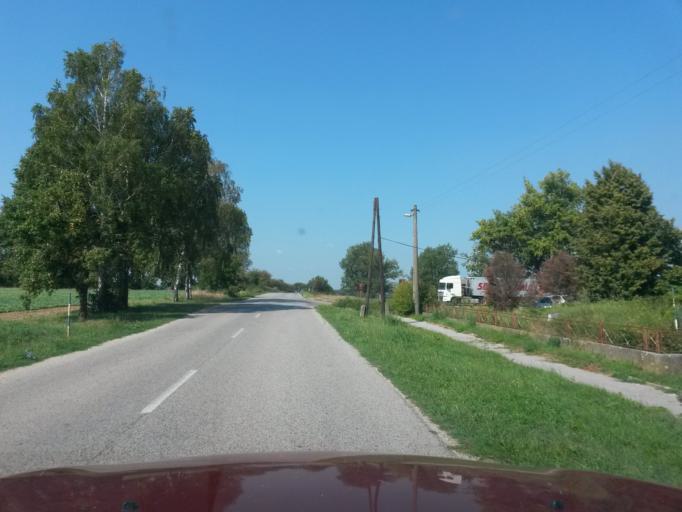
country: HU
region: Borsod-Abauj-Zemplen
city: Gonc
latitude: 48.5344
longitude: 21.1789
